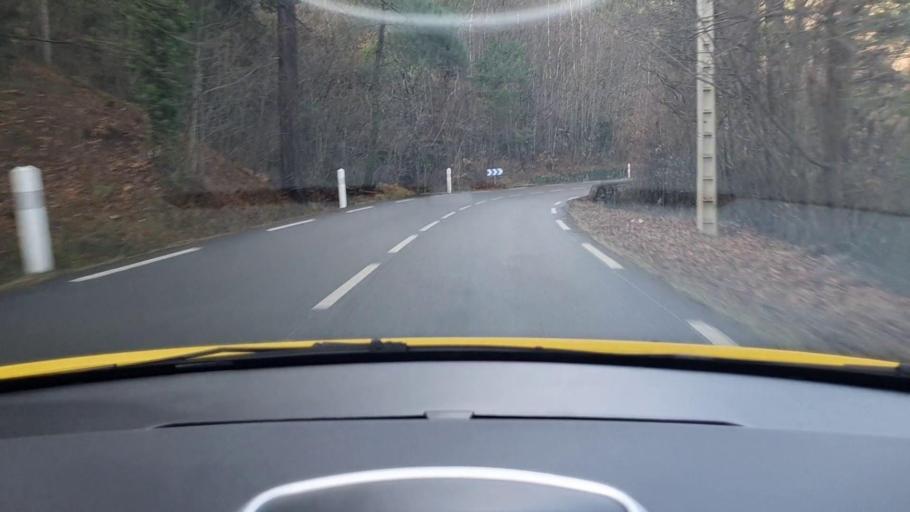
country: FR
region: Languedoc-Roussillon
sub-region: Departement du Gard
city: Branoux-les-Taillades
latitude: 44.2702
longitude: 4.0190
